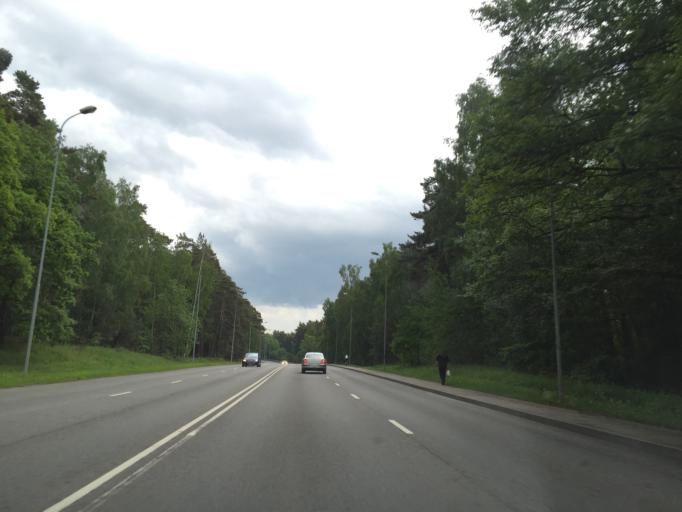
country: LT
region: Klaipedos apskritis
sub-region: Klaipeda
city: Klaipeda
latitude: 55.7364
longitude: 21.0981
